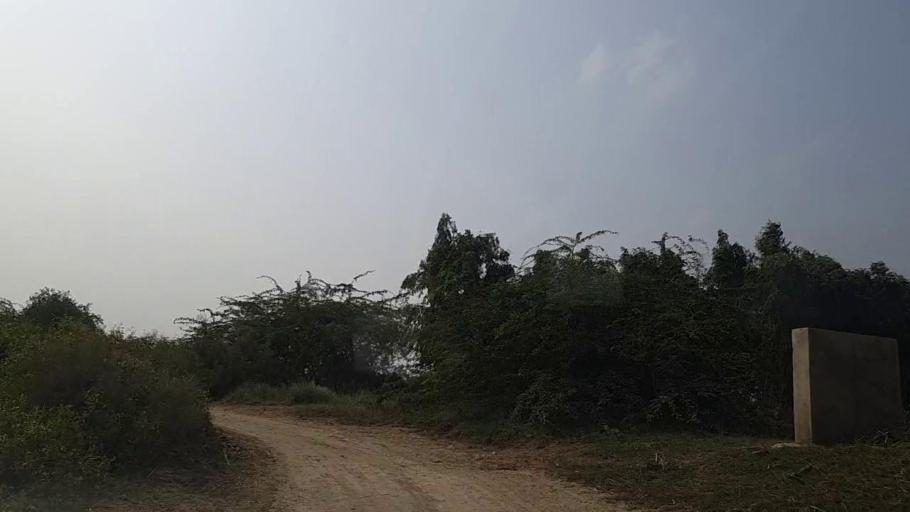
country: PK
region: Sindh
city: Mirpur Sakro
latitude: 24.6492
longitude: 67.7667
